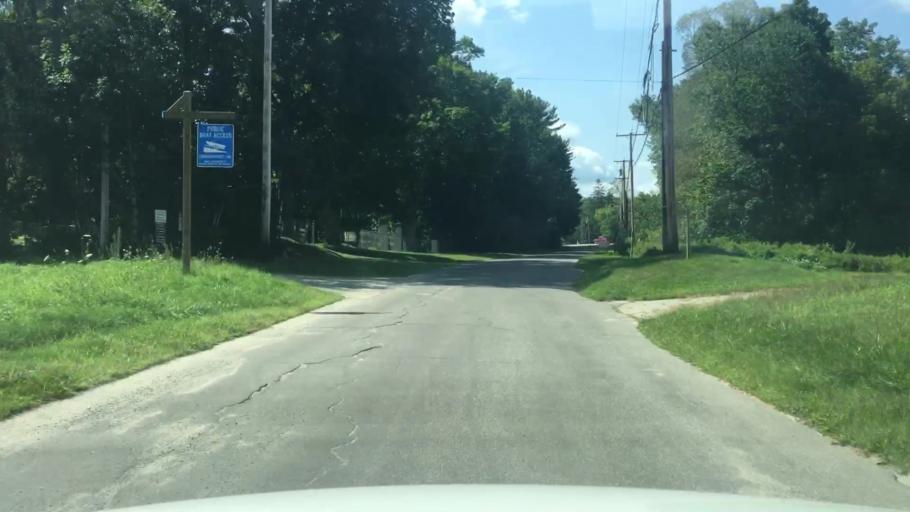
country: US
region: Maine
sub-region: Kennebec County
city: Manchester
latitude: 44.3210
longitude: -69.8948
